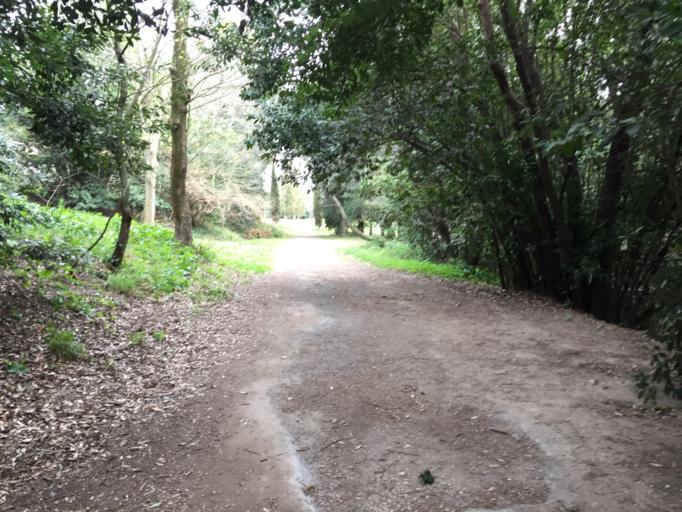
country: VA
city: Vatican City
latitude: 41.8836
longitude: 12.4460
